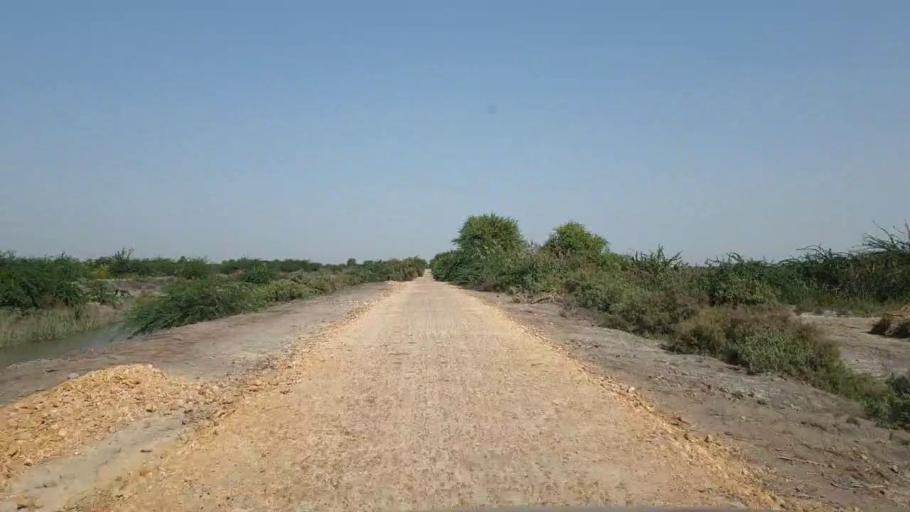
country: PK
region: Sindh
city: Tando Bago
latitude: 24.7240
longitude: 69.0734
